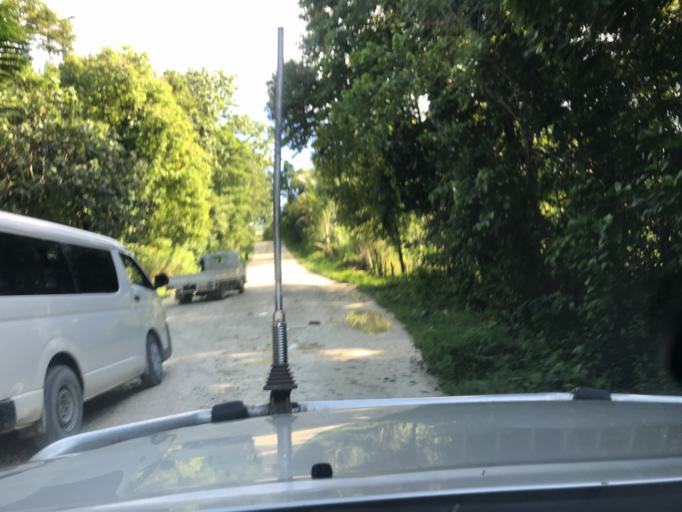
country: SB
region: Malaita
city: Auki
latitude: -8.7031
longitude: 160.6994
